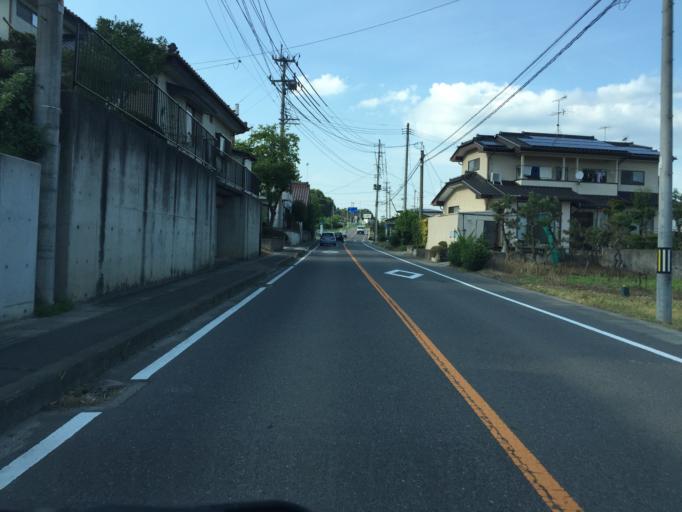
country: JP
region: Fukushima
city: Nihommatsu
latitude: 37.5663
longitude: 140.4133
